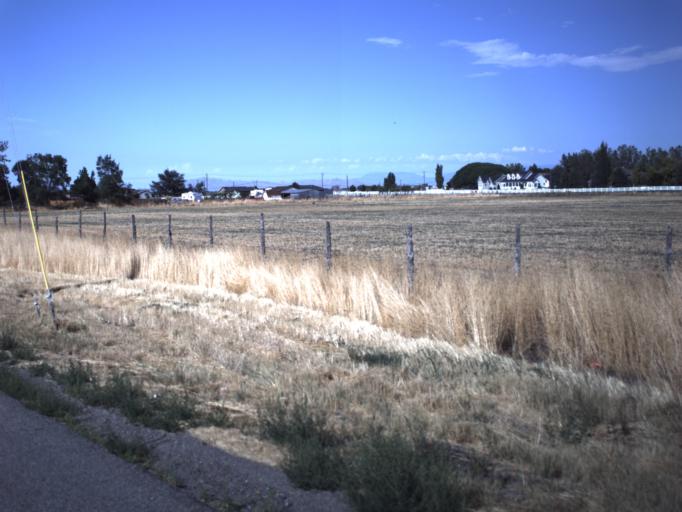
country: US
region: Utah
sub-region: Tooele County
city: Grantsville
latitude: 40.5960
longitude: -112.4259
